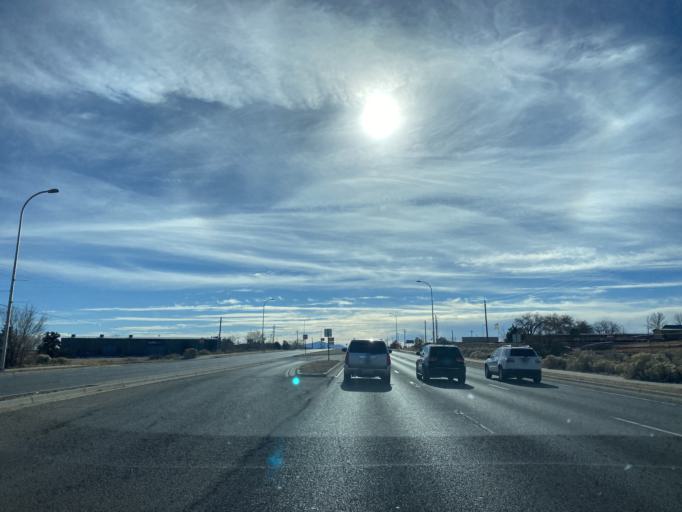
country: US
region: New Mexico
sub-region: Santa Fe County
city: Agua Fria
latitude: 35.6271
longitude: -106.0248
